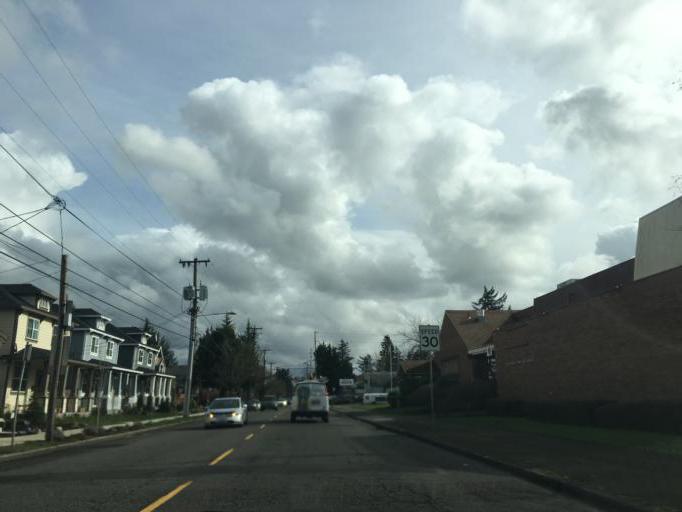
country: US
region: Oregon
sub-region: Multnomah County
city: Lents
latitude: 45.4903
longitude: -122.5939
